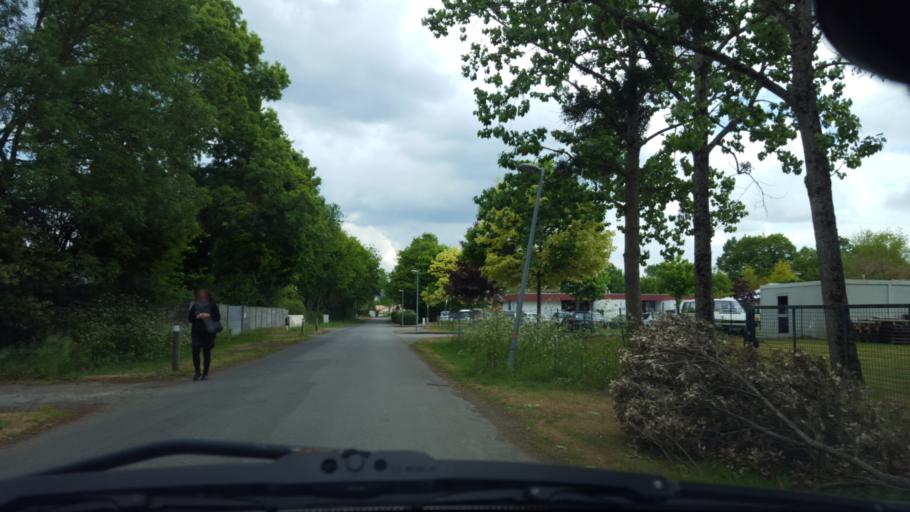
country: FR
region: Pays de la Loire
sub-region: Departement de la Loire-Atlantique
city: Saint-Philbert-de-Grand-Lieu
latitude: 47.0450
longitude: -1.6415
